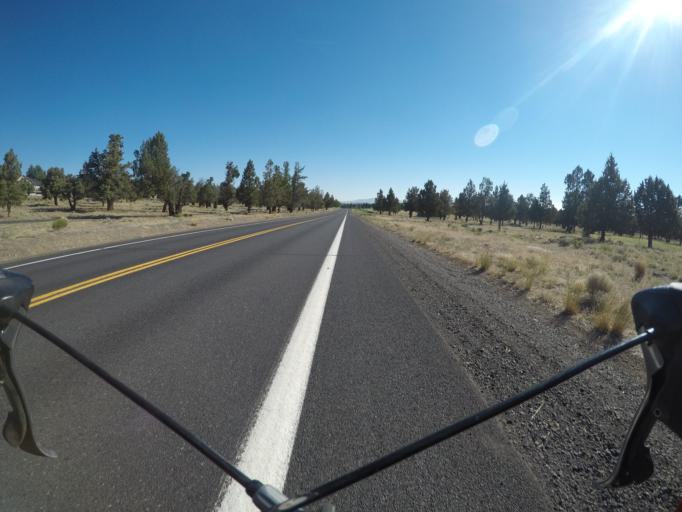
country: US
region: Oregon
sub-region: Deschutes County
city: Redmond
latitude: 44.2577
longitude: -121.2681
